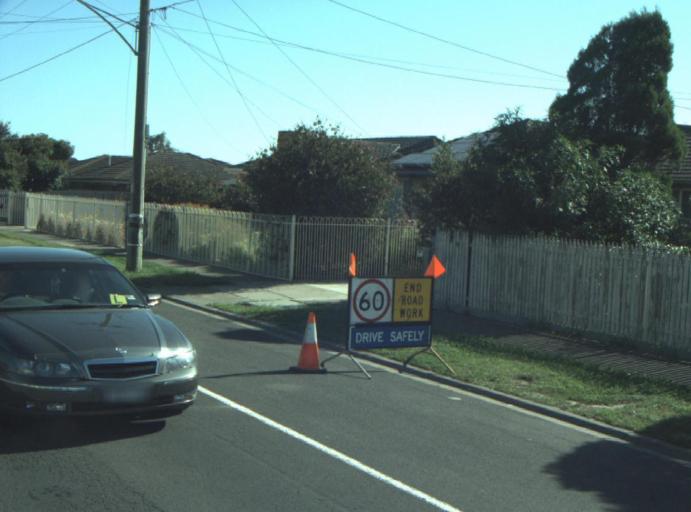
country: AU
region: Victoria
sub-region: Greater Geelong
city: Bell Post Hill
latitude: -38.1028
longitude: 144.3225
